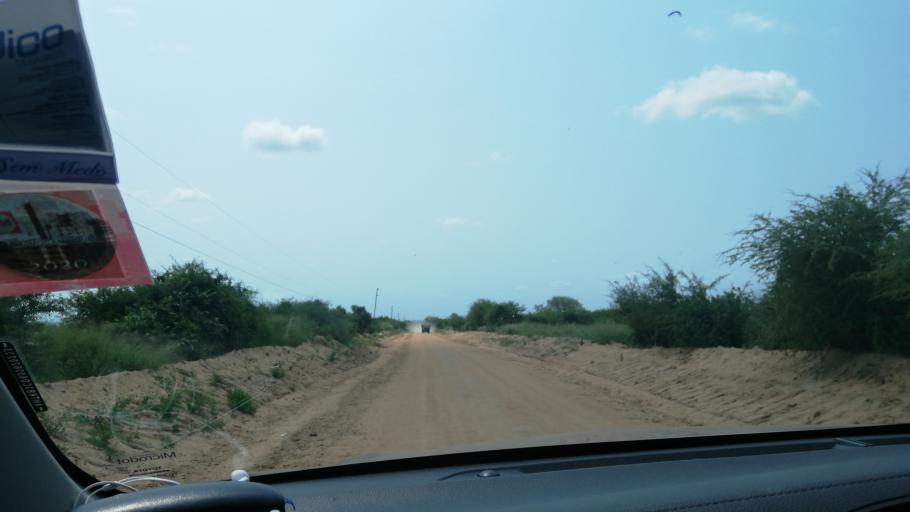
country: MZ
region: Maputo
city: Matola
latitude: -26.0944
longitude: 32.3897
